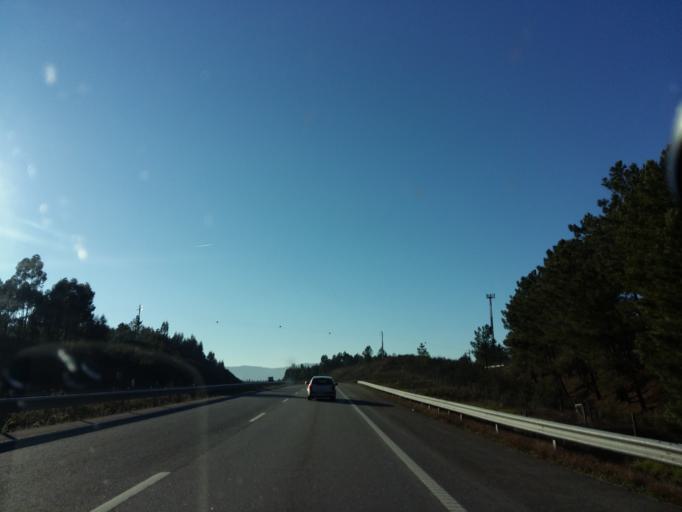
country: ES
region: Extremadura
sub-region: Provincia de Caceres
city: Cedillo
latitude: 39.7323
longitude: -7.6724
